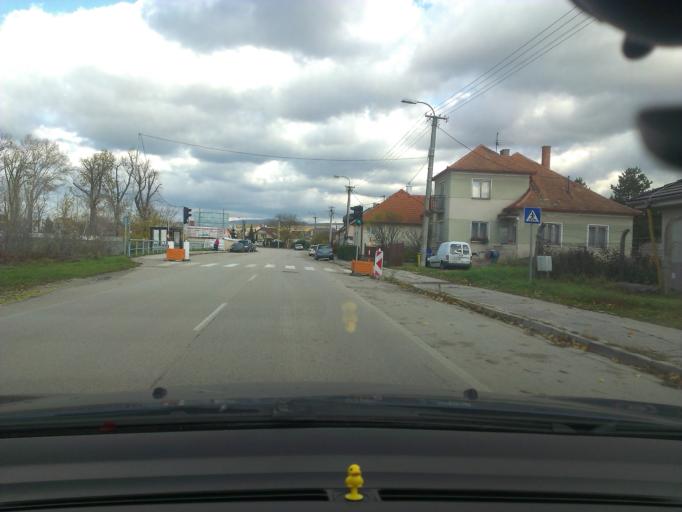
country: SK
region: Trnavsky
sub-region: Okres Trnava
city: Piestany
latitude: 48.5871
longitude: 17.8553
